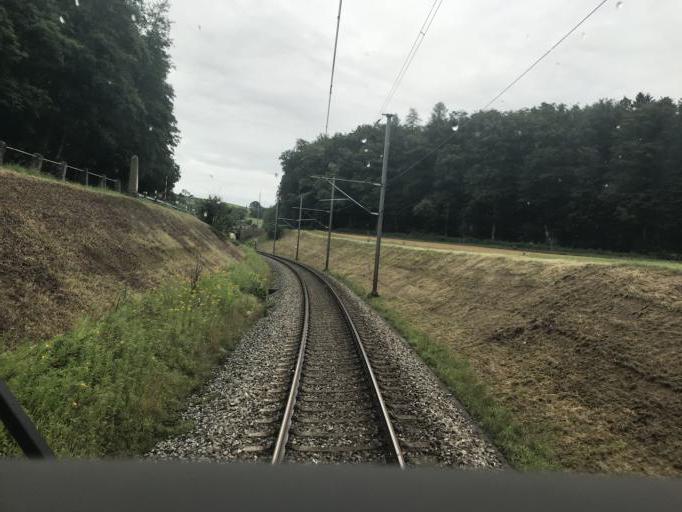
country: DE
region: Baden-Wuerttemberg
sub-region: Freiburg Region
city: Lottstetten
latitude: 47.6197
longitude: 8.5610
